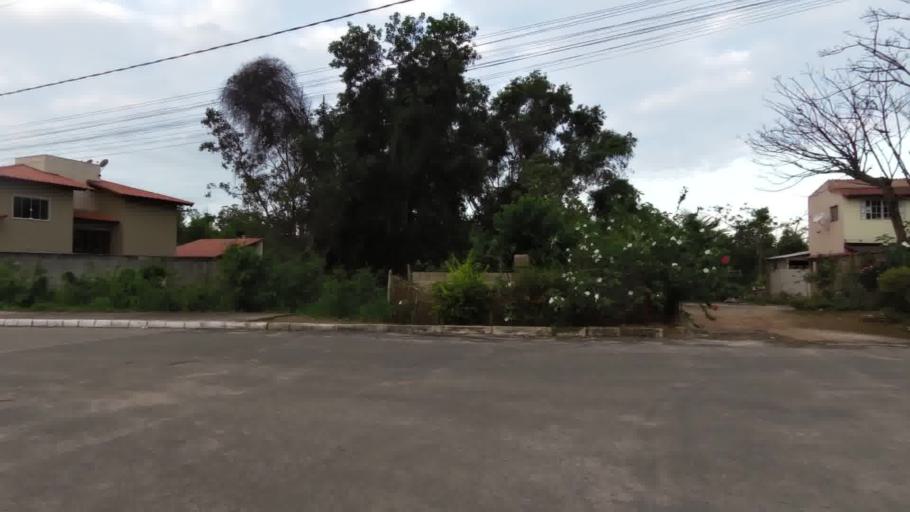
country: BR
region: Espirito Santo
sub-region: Piuma
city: Piuma
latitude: -20.8112
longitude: -40.6296
